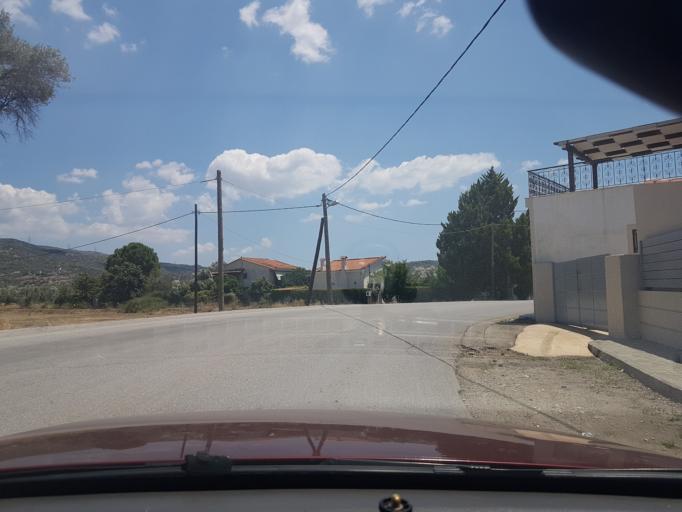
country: GR
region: Central Greece
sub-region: Nomos Evvoias
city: Afration
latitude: 38.4539
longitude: 23.6774
